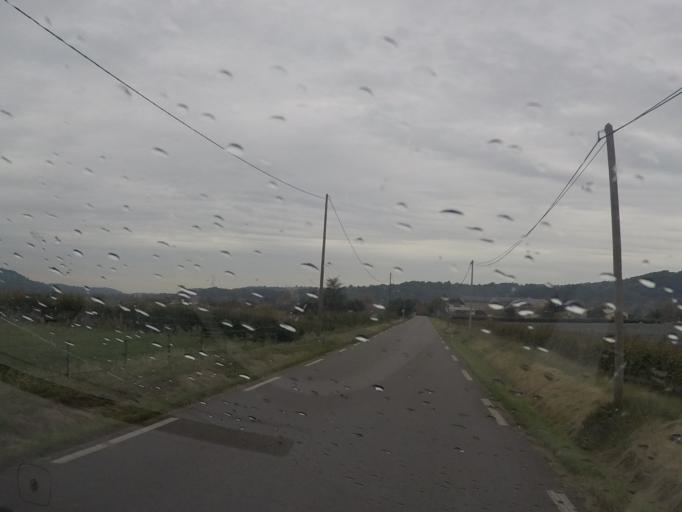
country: FR
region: Provence-Alpes-Cote d'Azur
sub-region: Departement du Vaucluse
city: Bonnieux
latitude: 43.8513
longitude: 5.2807
